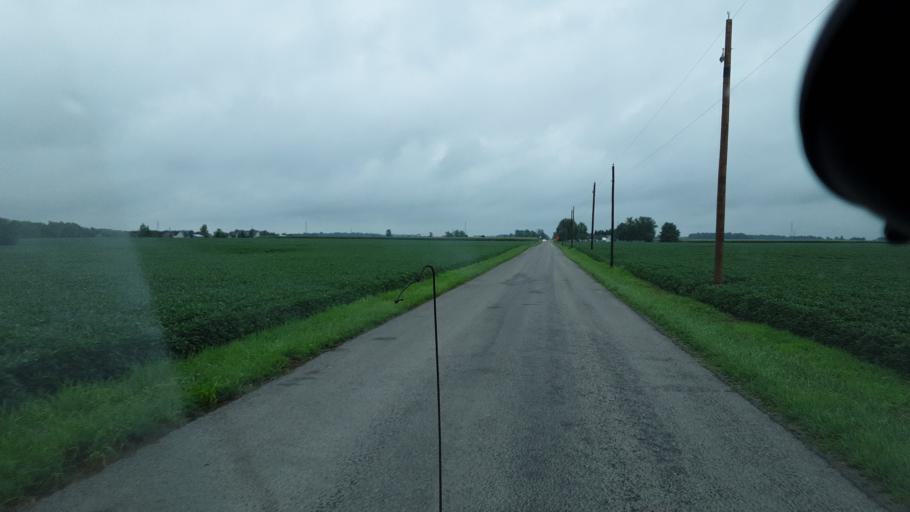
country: US
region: Indiana
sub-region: Wells County
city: Ossian
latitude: 40.9368
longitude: -85.1100
